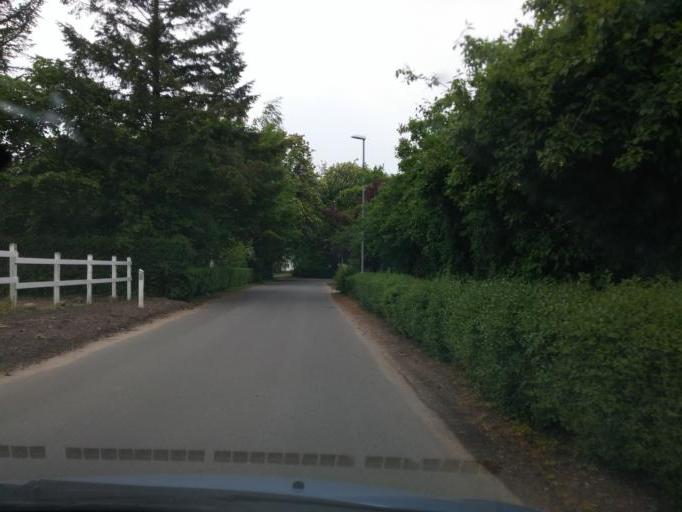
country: DK
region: South Denmark
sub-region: Odense Kommune
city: Bullerup
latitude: 55.4095
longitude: 10.5074
